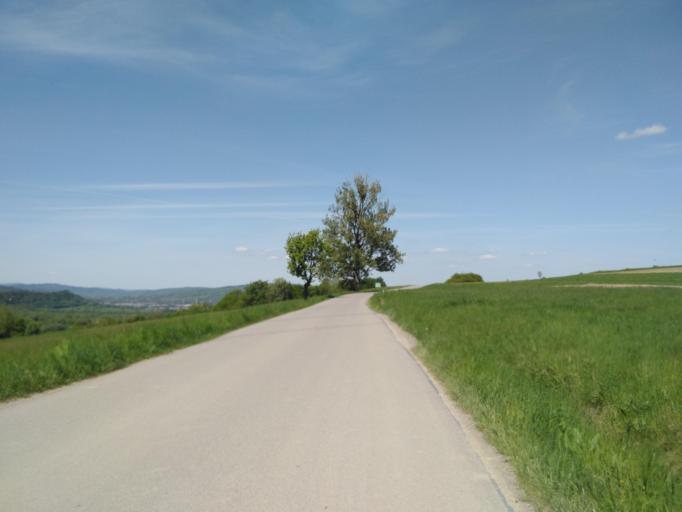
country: PL
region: Subcarpathian Voivodeship
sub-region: Powiat krosnienski
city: Iwonicz-Zdroj
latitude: 49.5370
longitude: 21.7484
